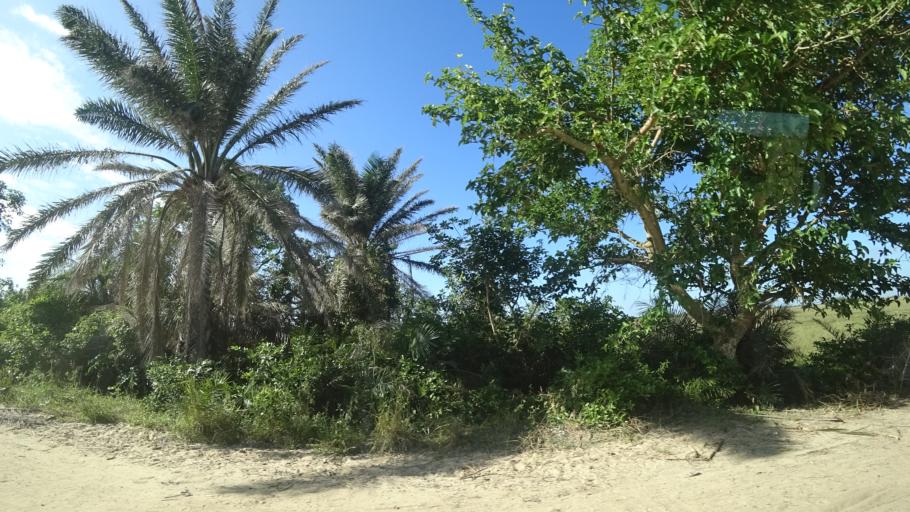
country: MZ
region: Sofala
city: Beira
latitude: -19.7318
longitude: 34.9789
